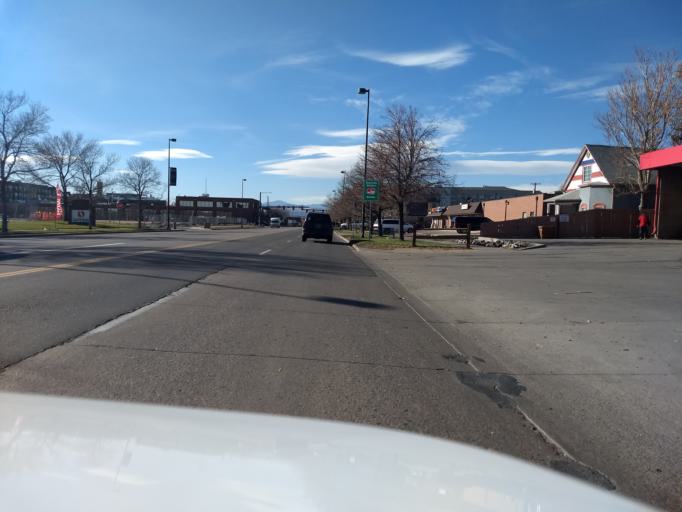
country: US
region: Colorado
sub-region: Denver County
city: Denver
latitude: 39.7113
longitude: -104.9903
